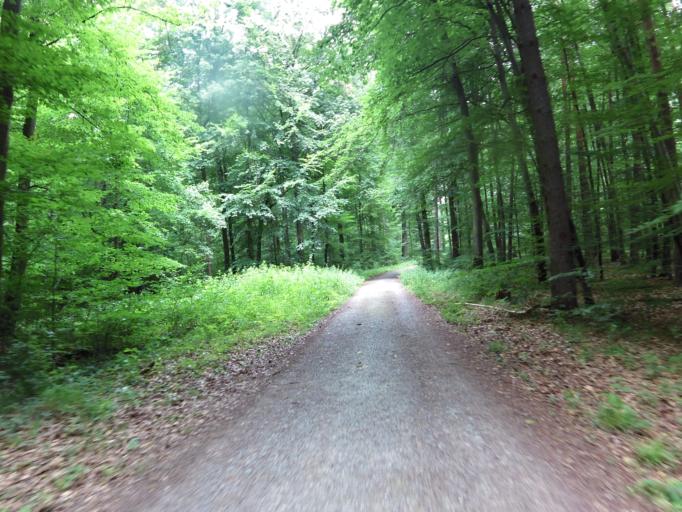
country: DE
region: Bavaria
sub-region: Regierungsbezirk Unterfranken
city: Reichenberg
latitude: 49.7589
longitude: 9.9092
